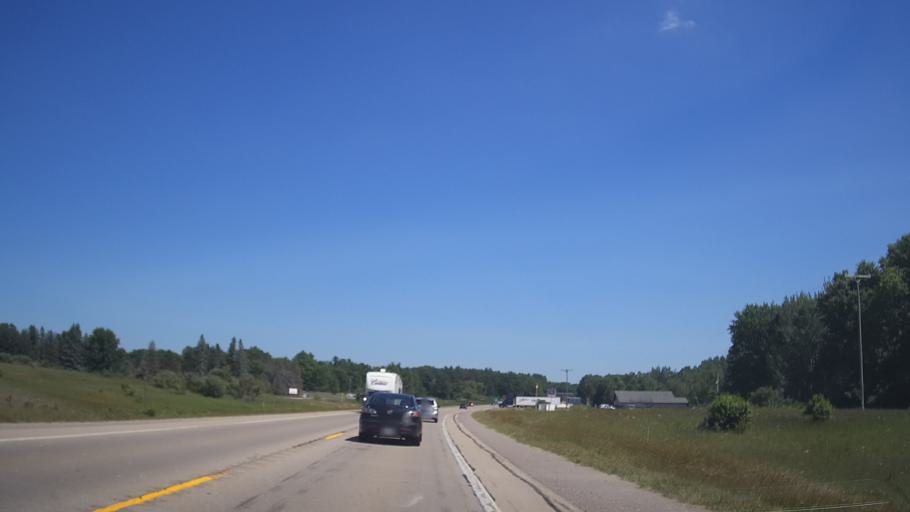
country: US
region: Michigan
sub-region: Clare County
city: Clare
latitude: 43.8689
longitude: -84.9186
